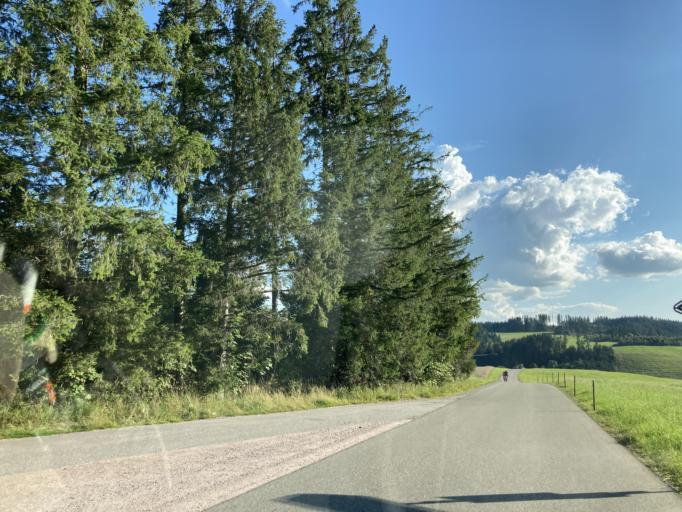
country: DE
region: Baden-Wuerttemberg
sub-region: Freiburg Region
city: Sankt Georgen im Schwarzwald
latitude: 48.1316
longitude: 8.2932
